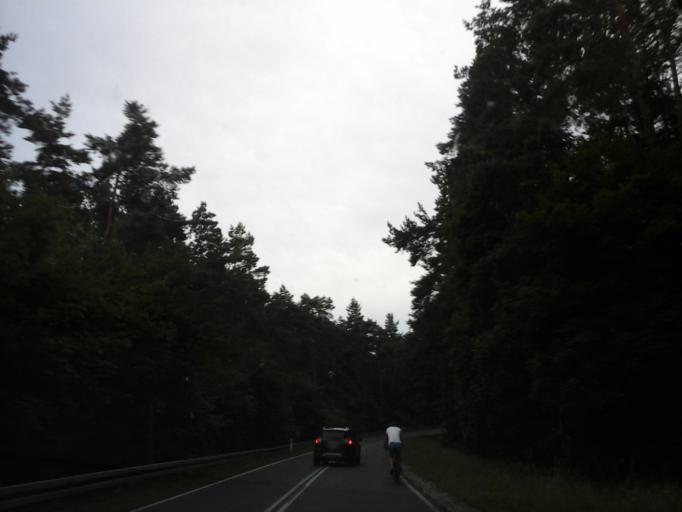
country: PL
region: West Pomeranian Voivodeship
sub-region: Powiat stargardzki
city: Stara Dabrowa
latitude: 53.4009
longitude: 15.1006
